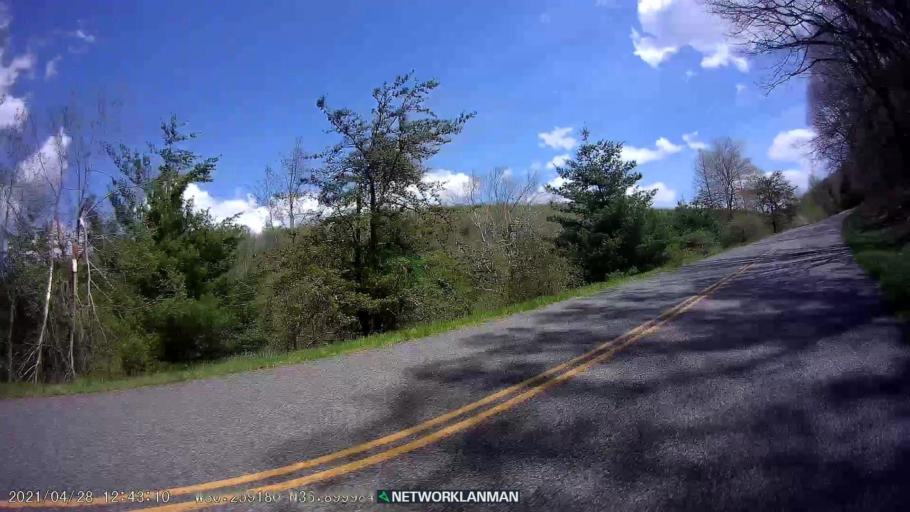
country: US
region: Virginia
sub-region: Floyd County
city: Floyd
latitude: 36.9000
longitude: -80.2590
